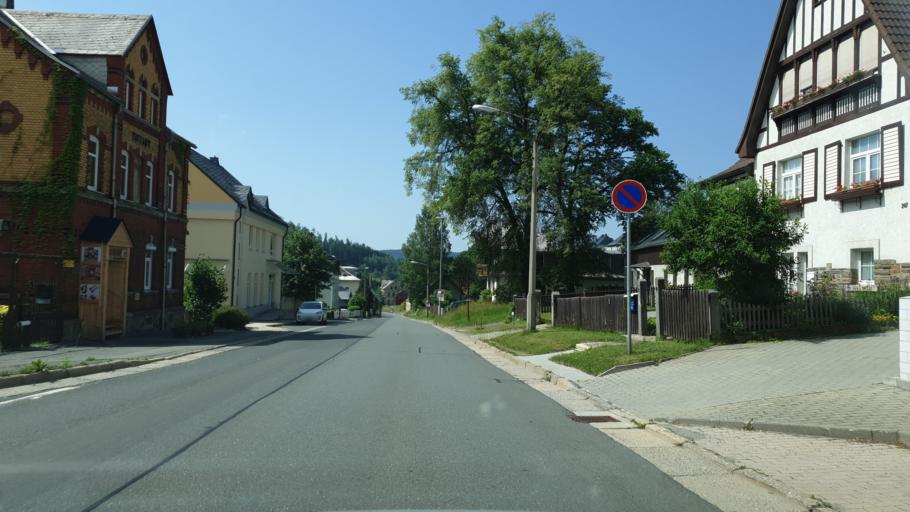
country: DE
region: Saxony
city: Klingenthal
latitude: 50.3807
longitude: 12.4819
